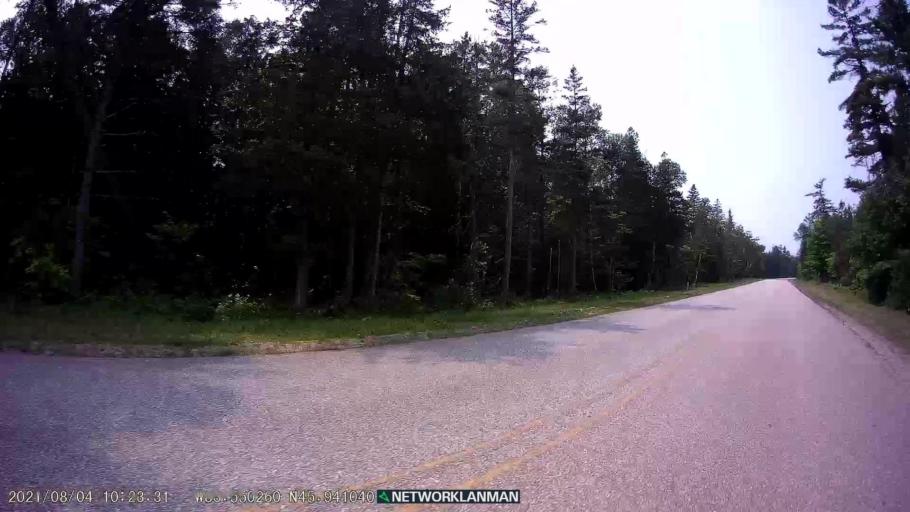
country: CA
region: Ontario
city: Thessalon
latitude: 45.9410
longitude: -83.5511
